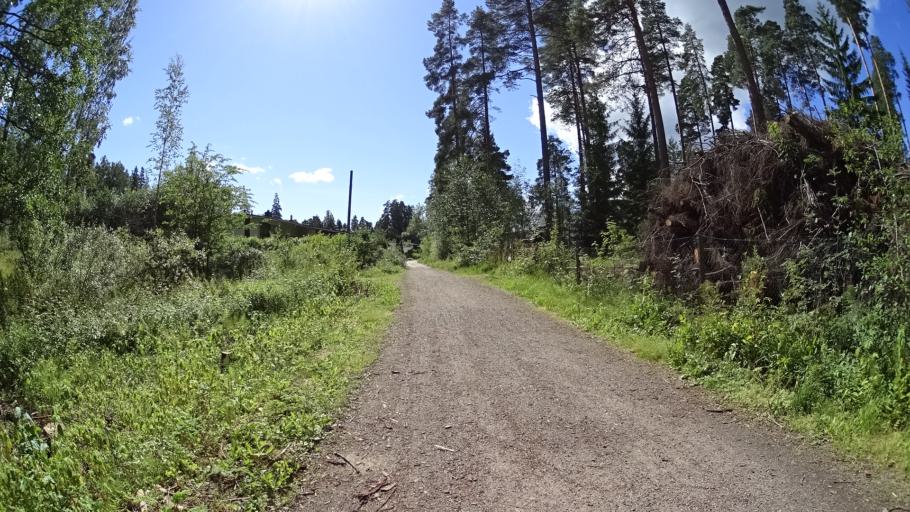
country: FI
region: Uusimaa
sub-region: Helsinki
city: Kauniainen
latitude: 60.2076
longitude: 24.7378
